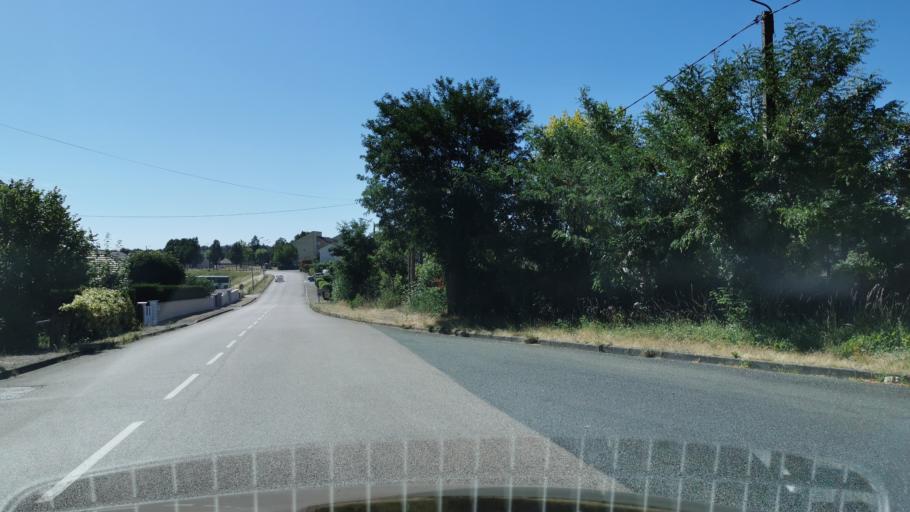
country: FR
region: Bourgogne
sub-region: Departement de Saone-et-Loire
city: Montchanin
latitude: 46.7605
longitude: 4.4762
